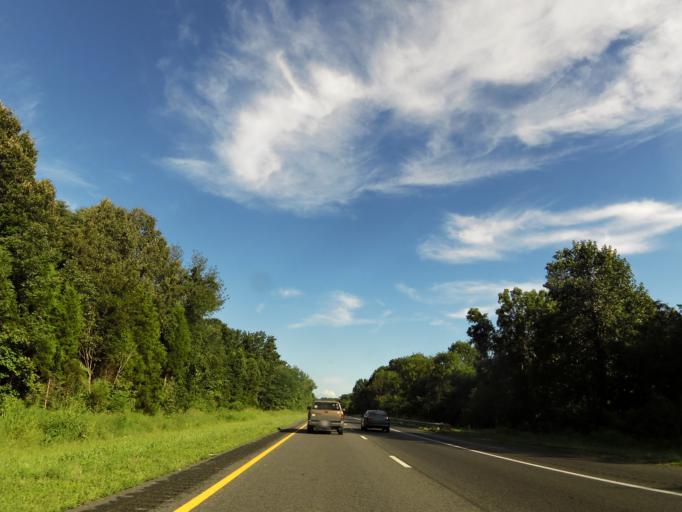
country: US
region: Kentucky
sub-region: Todd County
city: Guthrie
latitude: 36.5209
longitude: -87.2160
